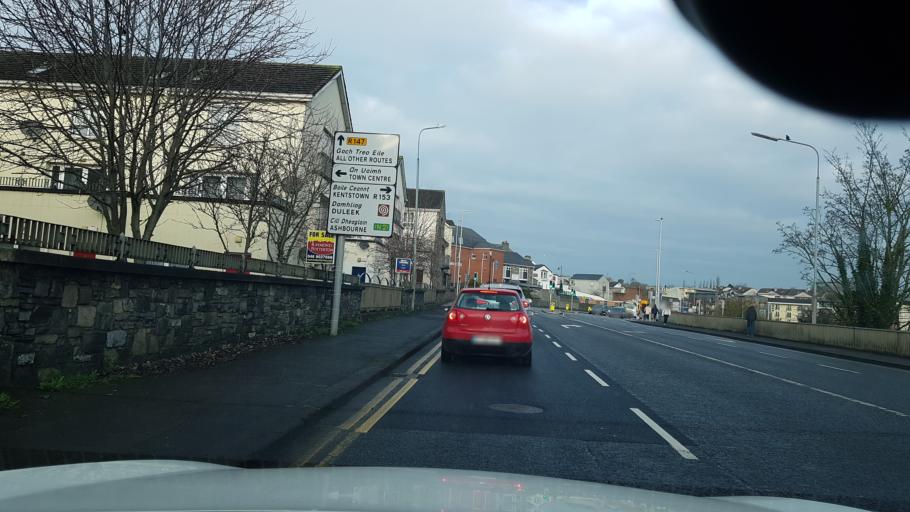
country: IE
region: Leinster
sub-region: An Mhi
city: Navan
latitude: 53.6524
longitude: -6.6820
